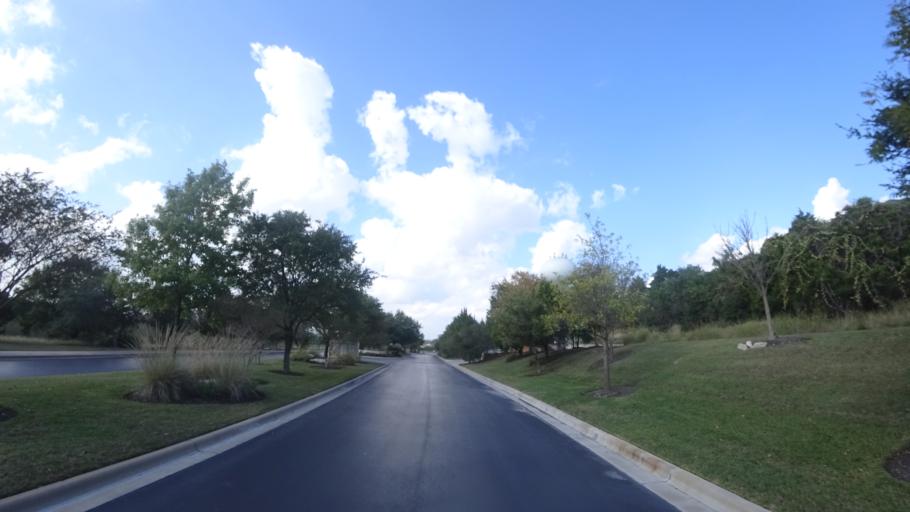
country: US
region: Texas
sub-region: Travis County
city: Barton Creek
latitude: 30.2910
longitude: -97.8661
